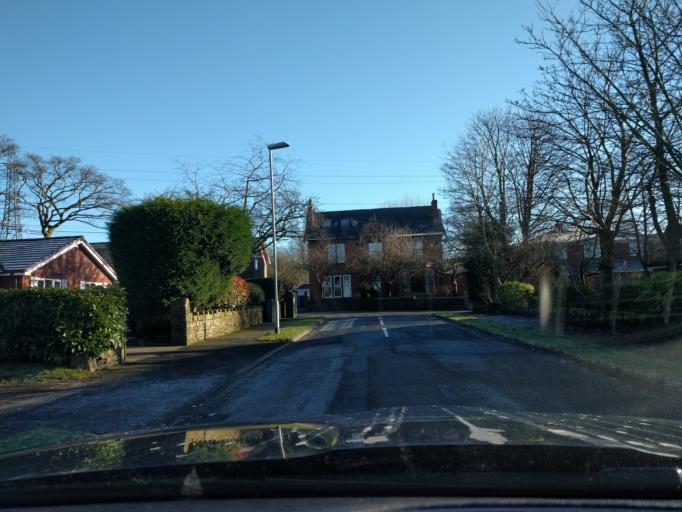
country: GB
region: England
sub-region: Borough of Tameside
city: Mossley
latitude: 53.5347
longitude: -2.0498
